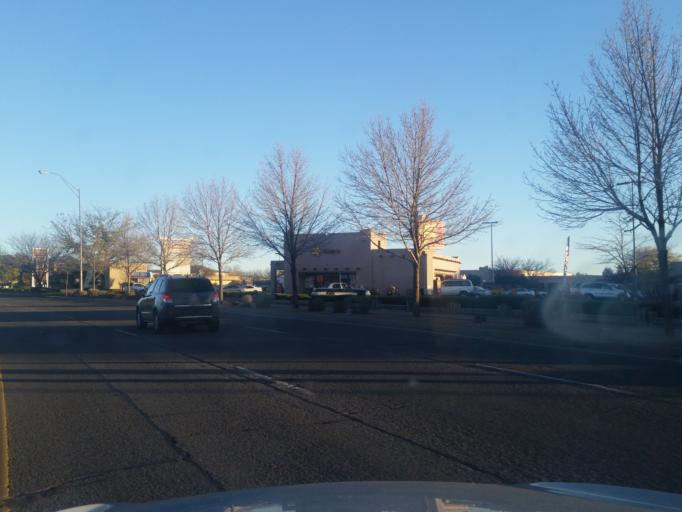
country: US
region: New Mexico
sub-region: Santa Fe County
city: Santa Fe
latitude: 35.6598
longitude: -105.9748
